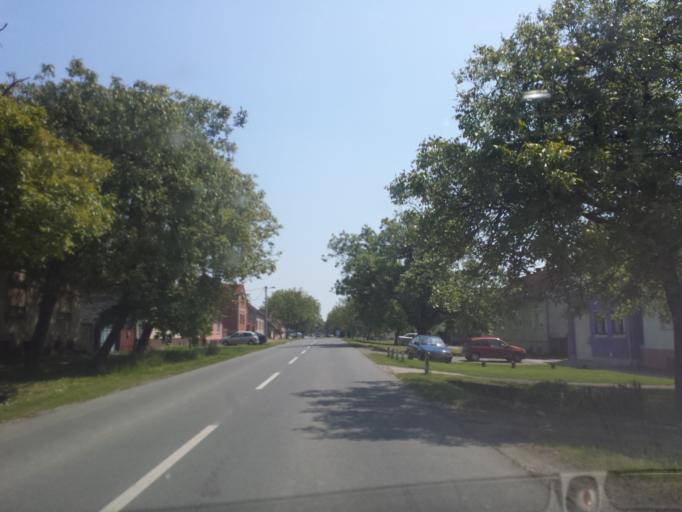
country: HR
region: Brodsko-Posavska
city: Oriovac
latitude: 45.1672
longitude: 17.7487
